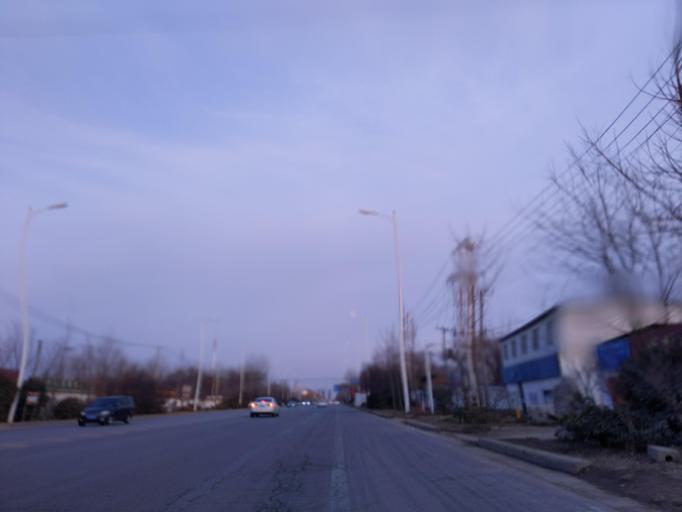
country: CN
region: Henan Sheng
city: Zhongyuanlu
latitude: 35.7869
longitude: 115.1239
